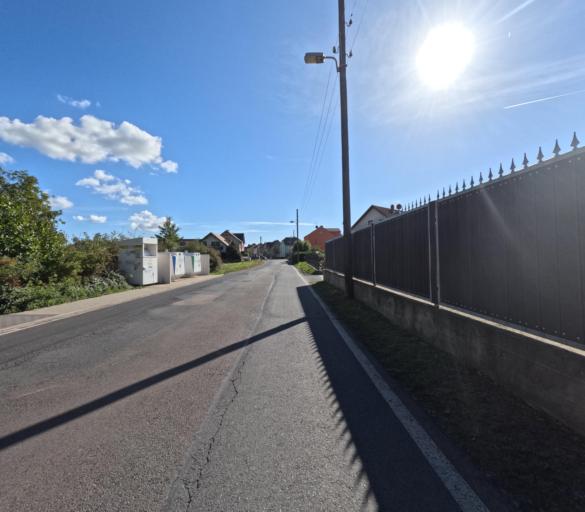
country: DE
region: Saxony
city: Moritzburg
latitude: 51.1206
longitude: 13.7213
